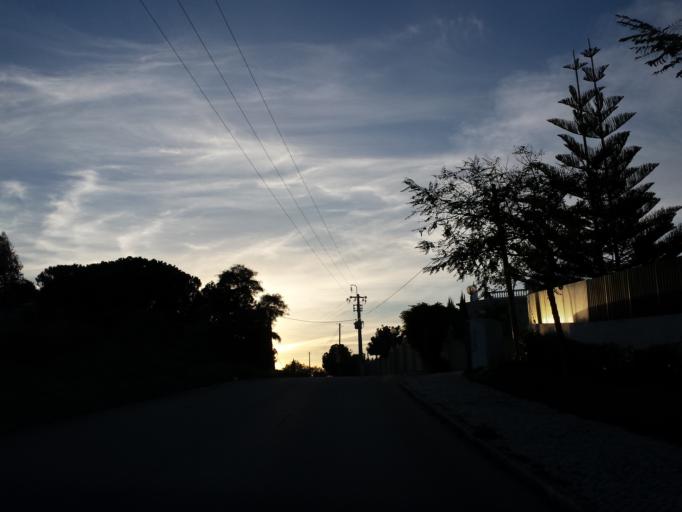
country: PT
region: Faro
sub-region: Lagos
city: Lagos
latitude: 37.1242
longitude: -8.6583
